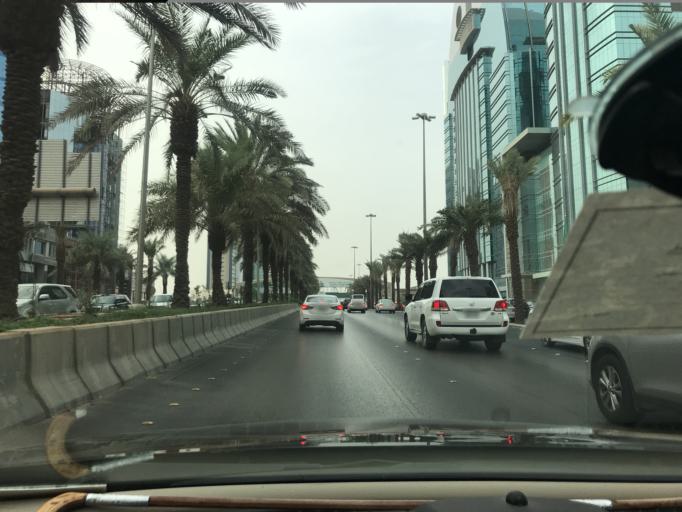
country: SA
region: Ar Riyad
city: Riyadh
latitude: 24.7054
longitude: 46.6755
